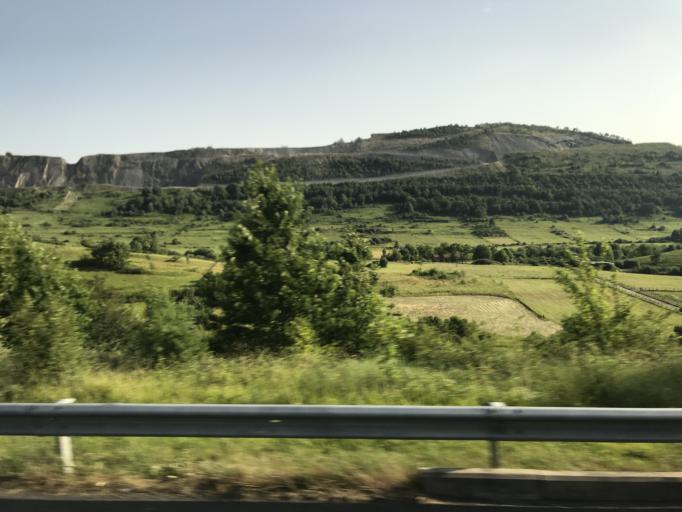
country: ES
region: Navarre
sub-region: Provincia de Navarra
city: Altsasu
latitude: 42.9161
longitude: -2.1920
